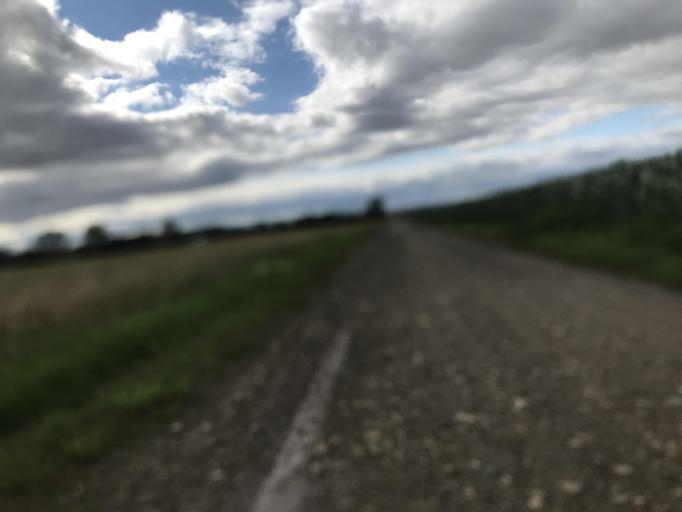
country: DE
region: Saxony-Anhalt
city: Ditfurt
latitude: 51.8149
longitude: 11.2302
